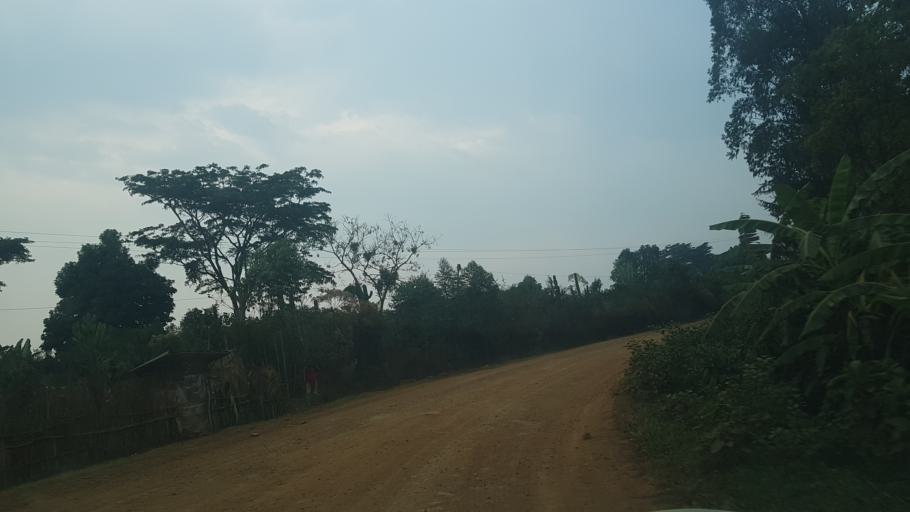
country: ET
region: Oromiya
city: Gore
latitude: 7.8965
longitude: 35.4912
